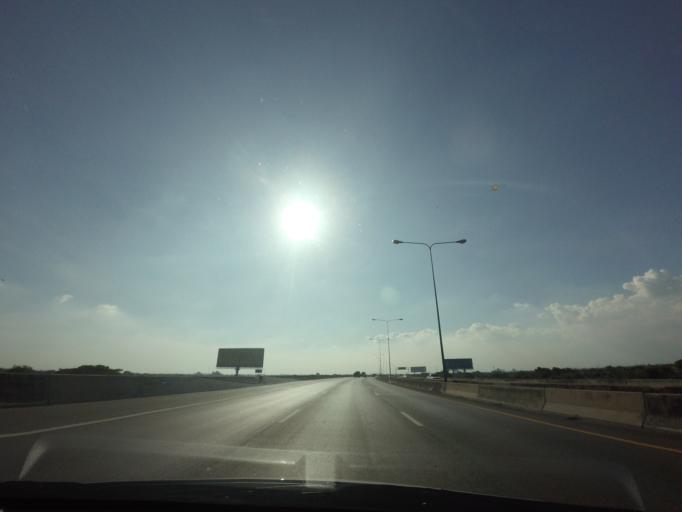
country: TH
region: Samut Prakan
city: Samut Prakan
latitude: 13.6007
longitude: 100.6493
